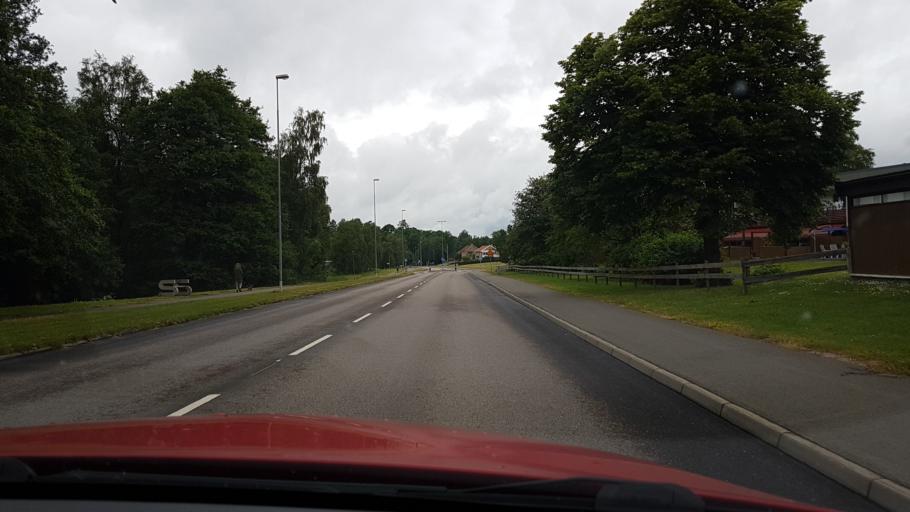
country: SE
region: Vaestra Goetaland
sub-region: Skovde Kommun
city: Skultorp
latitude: 58.3713
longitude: 13.8294
